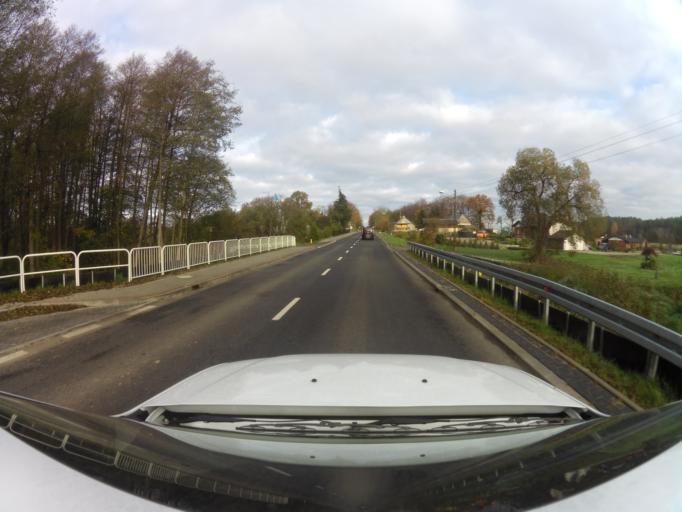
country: PL
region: West Pomeranian Voivodeship
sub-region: Powiat gryficki
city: Trzebiatow
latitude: 54.0144
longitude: 15.2438
